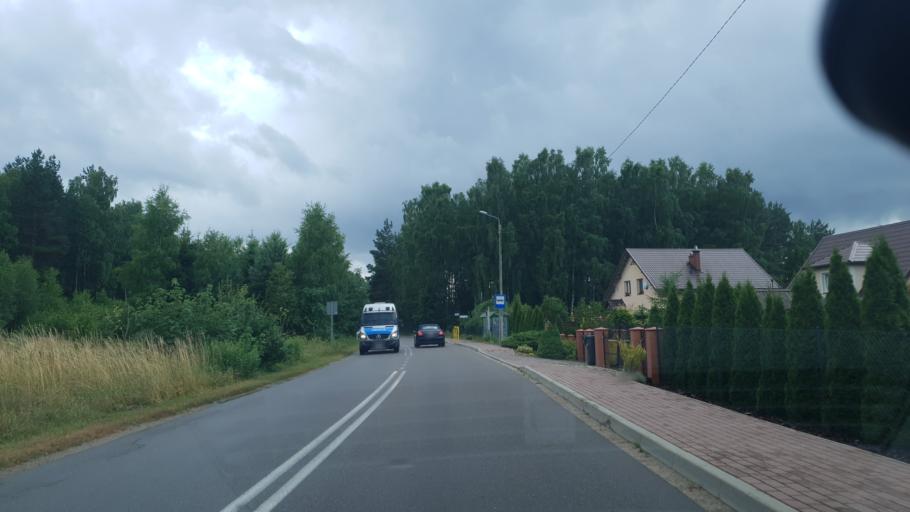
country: PL
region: Pomeranian Voivodeship
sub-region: Powiat kartuski
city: Stezyca
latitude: 54.2464
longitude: 18.0006
